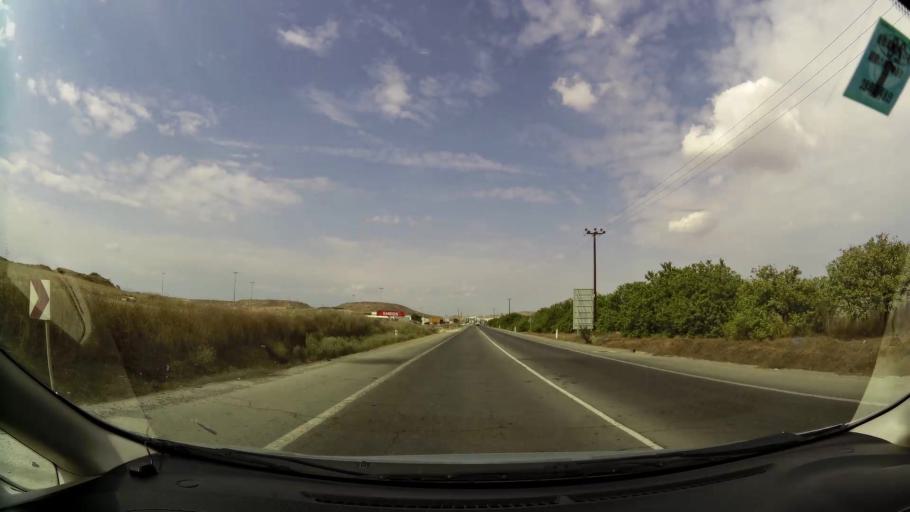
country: CY
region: Lefkosia
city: Dali
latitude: 35.0527
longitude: 33.3783
